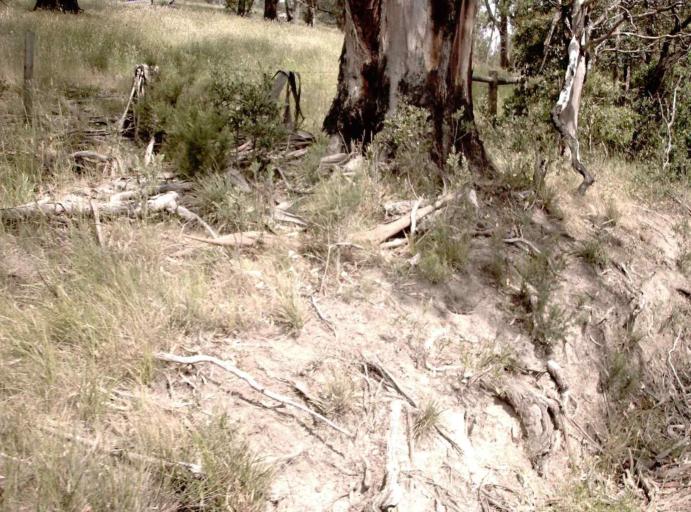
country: AU
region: Victoria
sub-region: Latrobe
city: Traralgon
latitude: -38.3209
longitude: 146.5694
